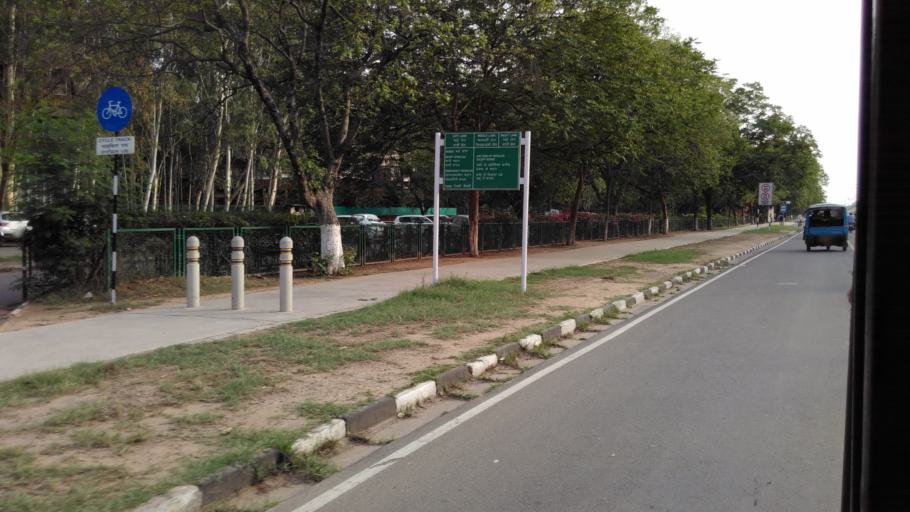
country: IN
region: Chandigarh
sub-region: Chandigarh
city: Chandigarh
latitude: 30.7497
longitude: 76.7907
